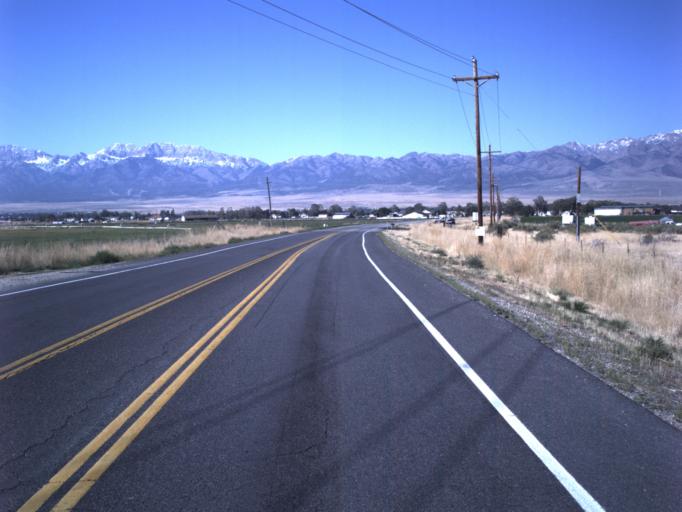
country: US
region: Utah
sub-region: Tooele County
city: Grantsville
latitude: 40.6009
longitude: -112.4066
